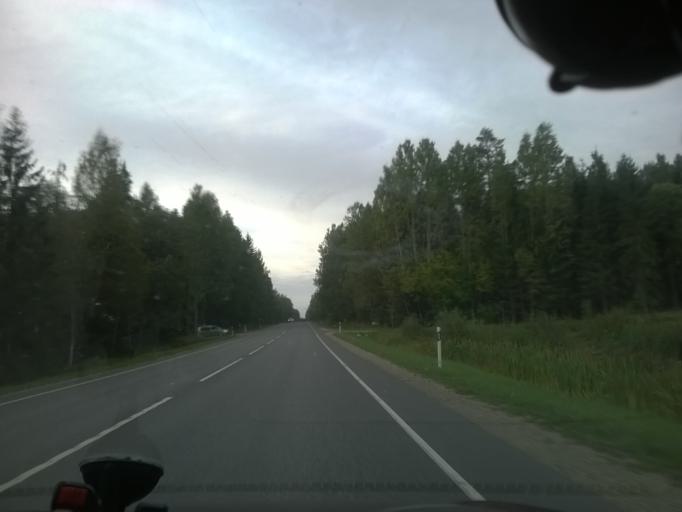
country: EE
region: Vorumaa
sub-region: Antsla vald
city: Vana-Antsla
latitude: 58.0167
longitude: 26.7479
